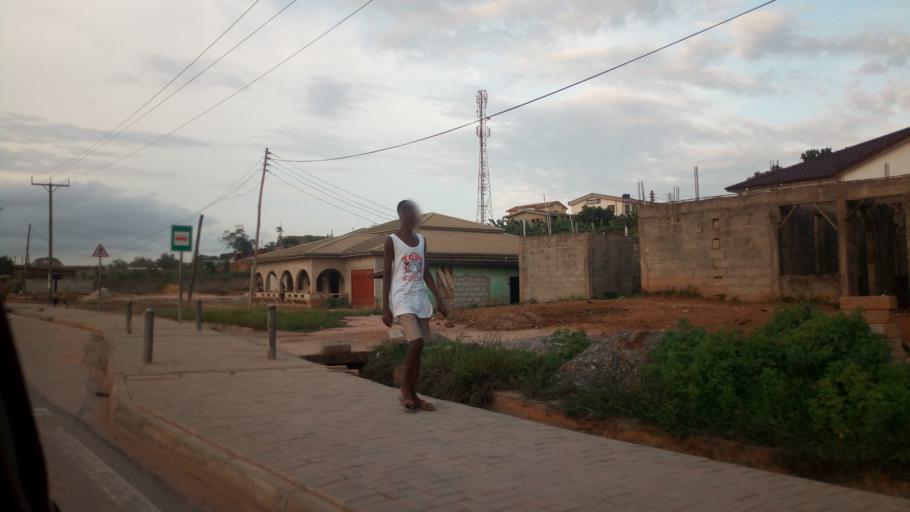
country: GH
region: Western
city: Sekondi-Takoradi
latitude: 4.9477
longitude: -1.7632
